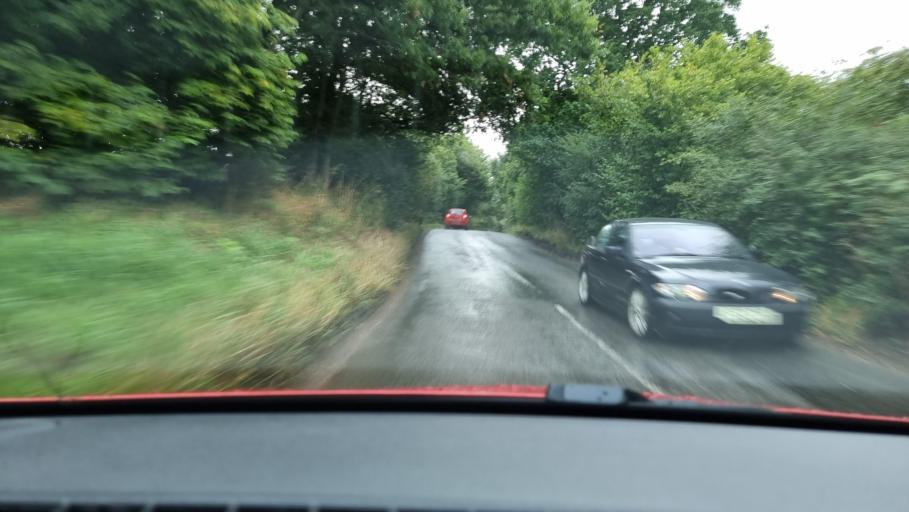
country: GB
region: England
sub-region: Buckinghamshire
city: Chesham
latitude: 51.7290
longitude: -0.5817
